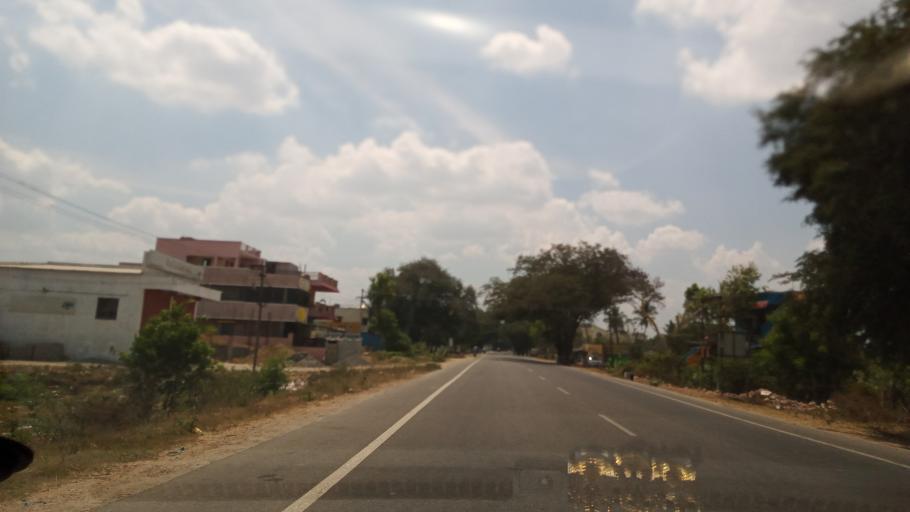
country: IN
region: Tamil Nadu
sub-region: Vellore
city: Walajapet
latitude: 12.9192
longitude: 79.3832
